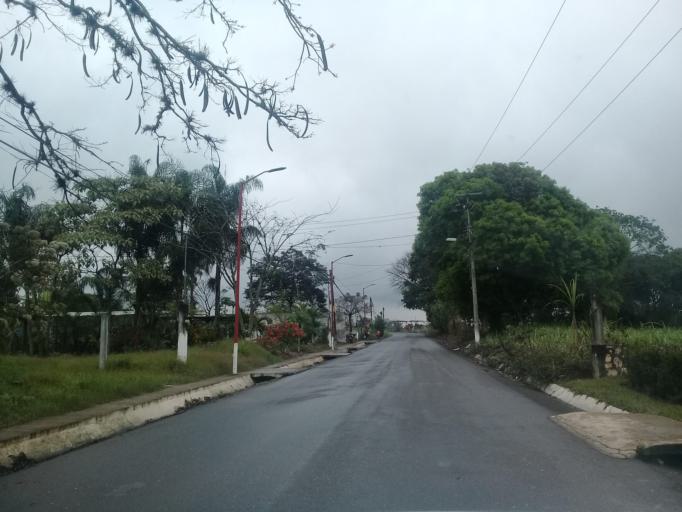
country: MX
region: Veracruz
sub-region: Amatlan de los Reyes
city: Trapiche Viejo
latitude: 18.8305
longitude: -96.9557
